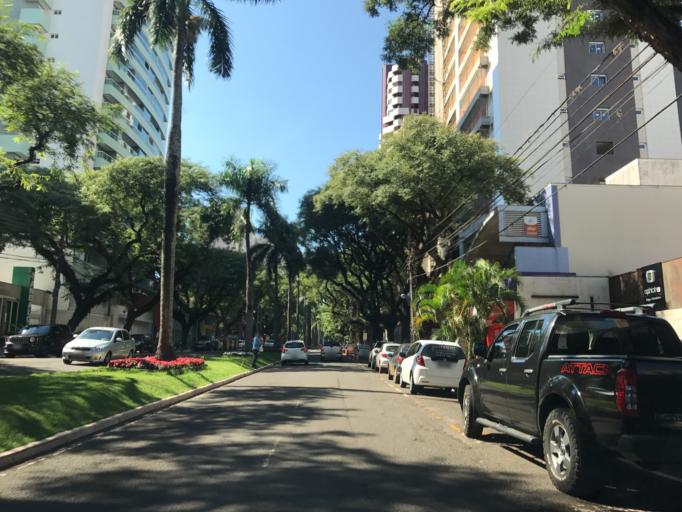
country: BR
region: Parana
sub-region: Maringa
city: Maringa
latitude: -23.4237
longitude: -51.9429
